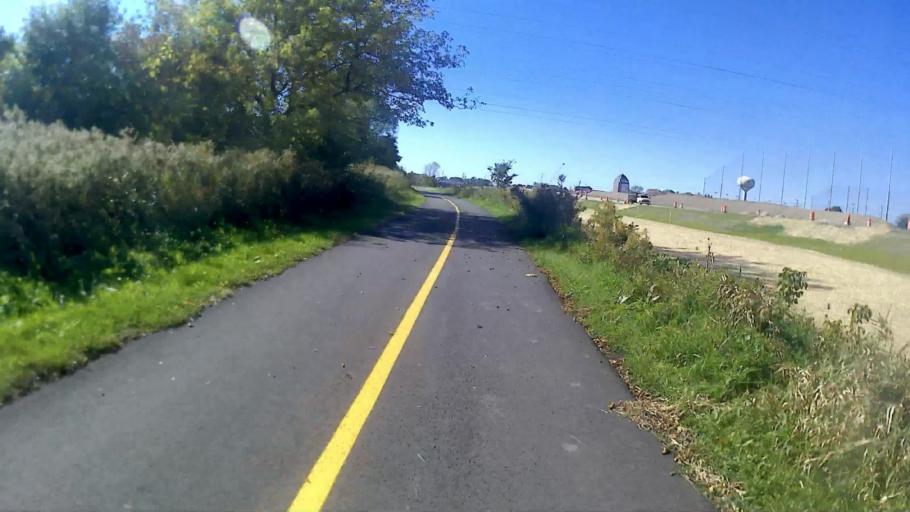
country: US
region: Illinois
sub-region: DuPage County
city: Itasca
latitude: 41.9828
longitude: -87.9923
